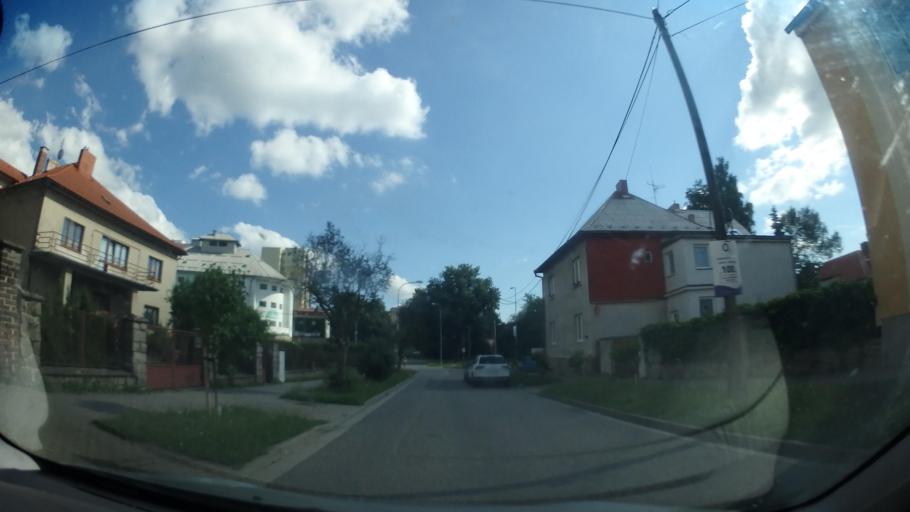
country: CZ
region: Vysocina
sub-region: Okres Zd'ar nad Sazavou
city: Zd'ar nad Sazavou
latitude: 49.5597
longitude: 15.9401
